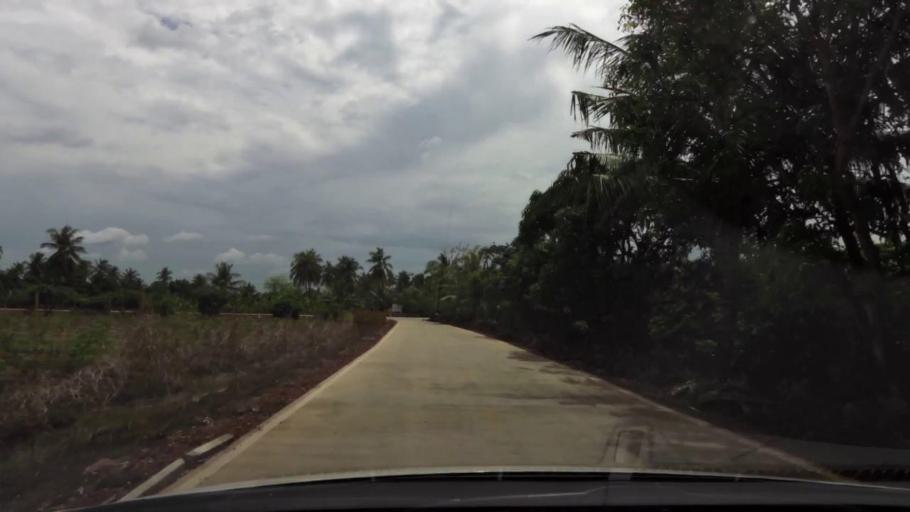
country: TH
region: Ratchaburi
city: Damnoen Saduak
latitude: 13.5471
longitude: 99.9856
